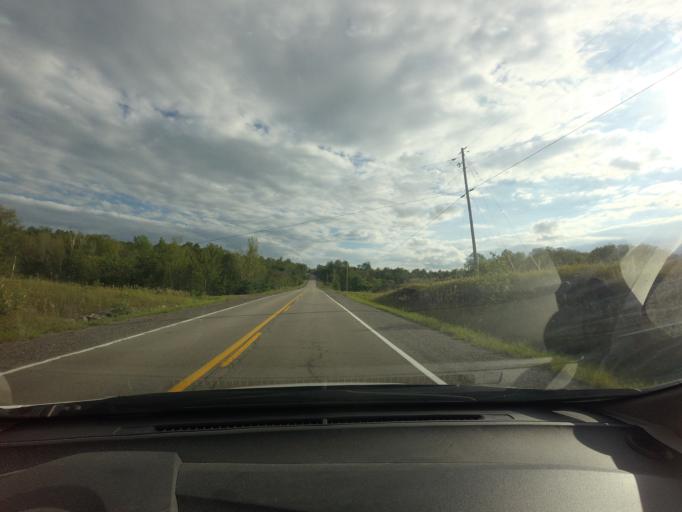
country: CA
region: Ontario
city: Perth
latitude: 44.7566
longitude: -76.3882
